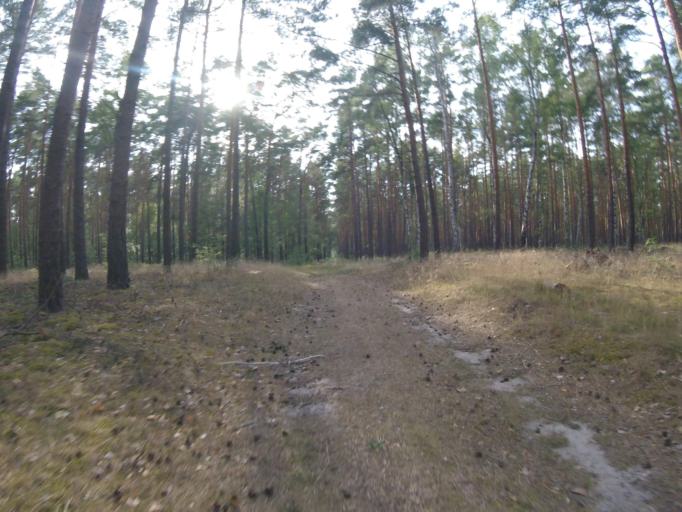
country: DE
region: Brandenburg
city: Gross Koris
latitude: 52.2102
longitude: 13.7369
